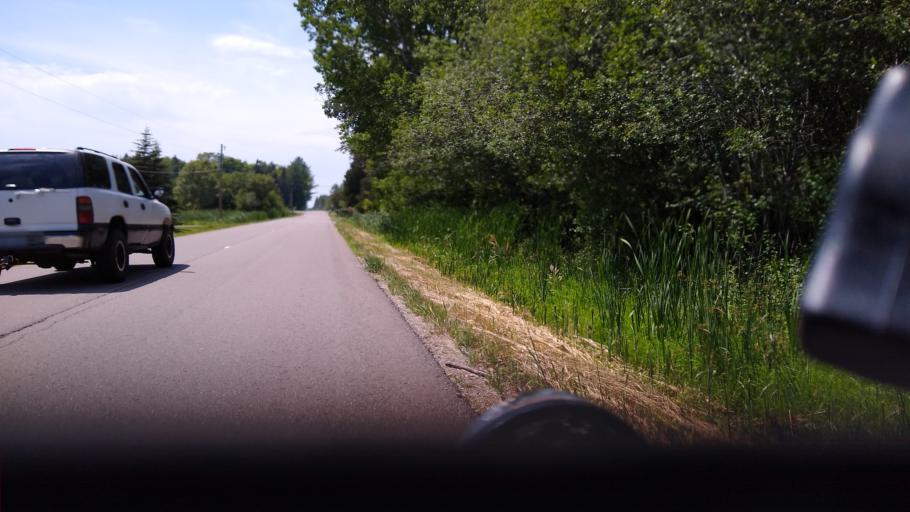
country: US
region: Michigan
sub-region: Delta County
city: Escanaba
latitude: 45.7101
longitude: -87.1180
